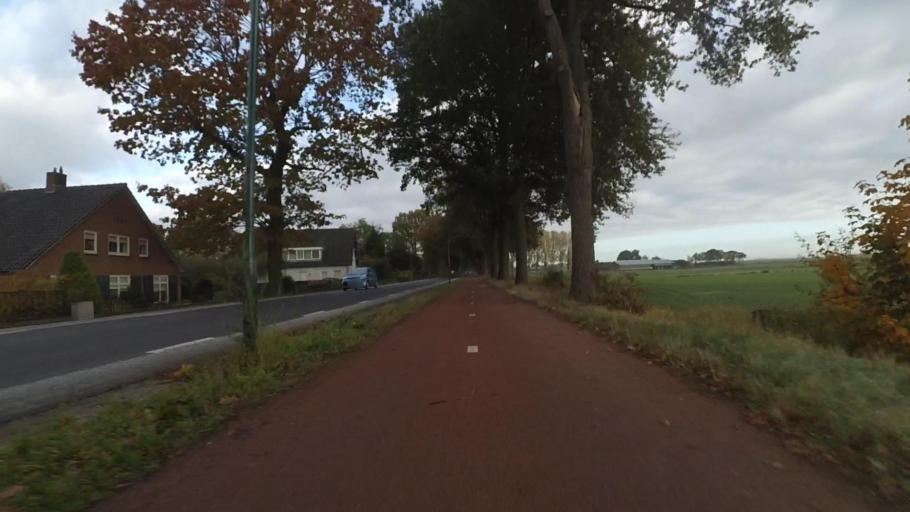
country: NL
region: Utrecht
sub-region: Gemeente Baarn
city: Baarn
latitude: 52.2383
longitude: 5.2613
